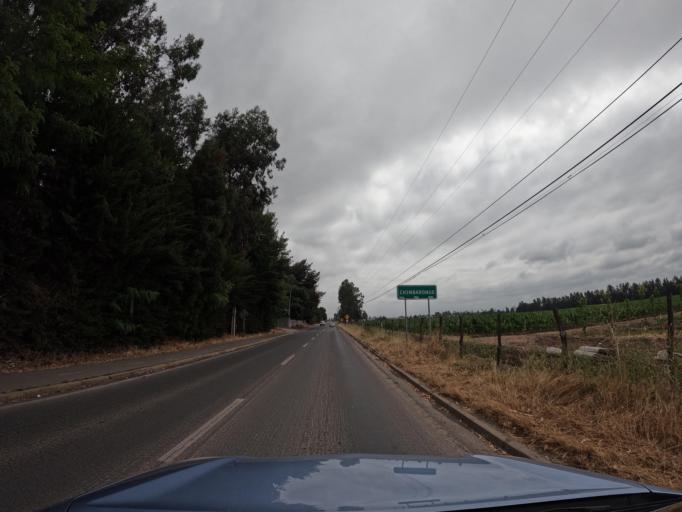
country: CL
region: O'Higgins
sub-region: Provincia de Colchagua
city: Chimbarongo
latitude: -34.7209
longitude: -71.0526
